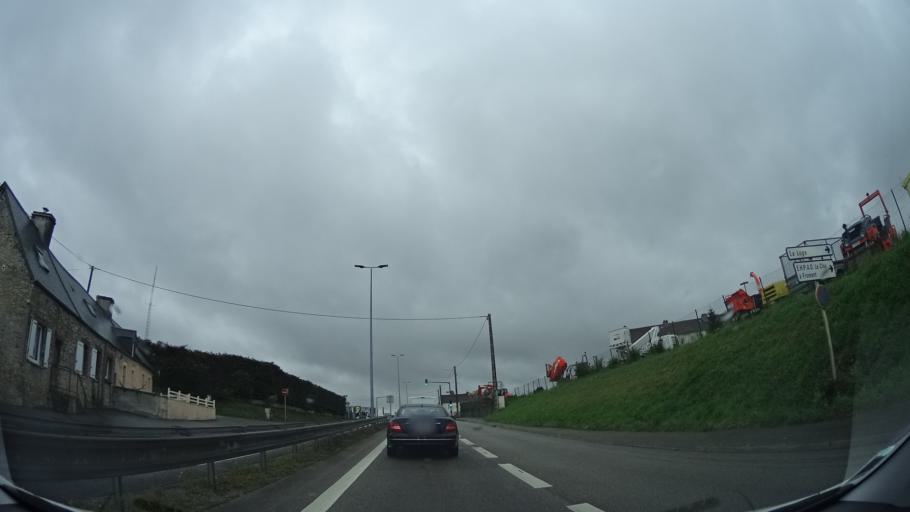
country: FR
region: Lower Normandy
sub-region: Departement de la Manche
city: La Glacerie
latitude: 49.6098
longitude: -1.6003
